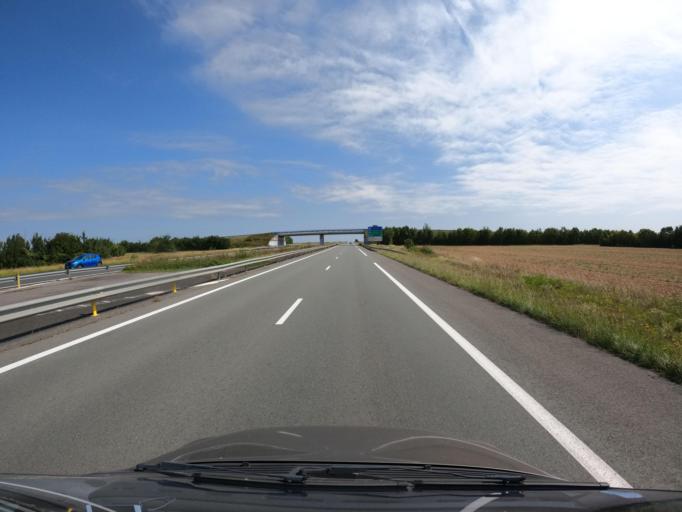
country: FR
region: Poitou-Charentes
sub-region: Departement des Deux-Sevres
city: Mauze-sur-le-Mignon
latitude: 46.2131
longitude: -0.6239
